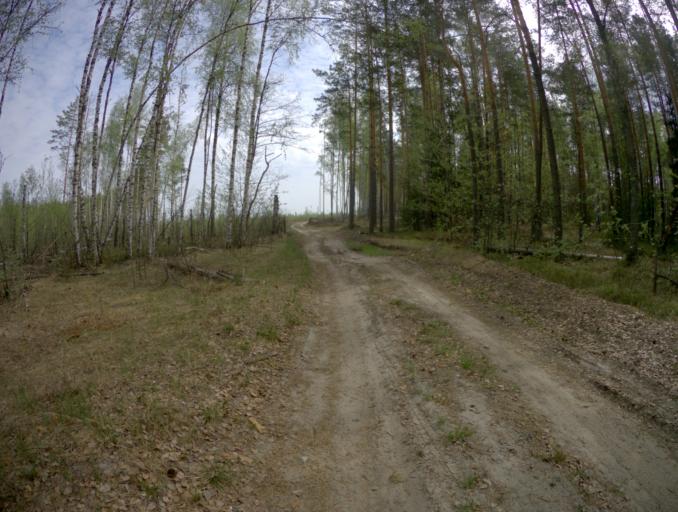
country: RU
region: Ivanovo
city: Talitsy
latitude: 56.4905
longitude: 42.1639
